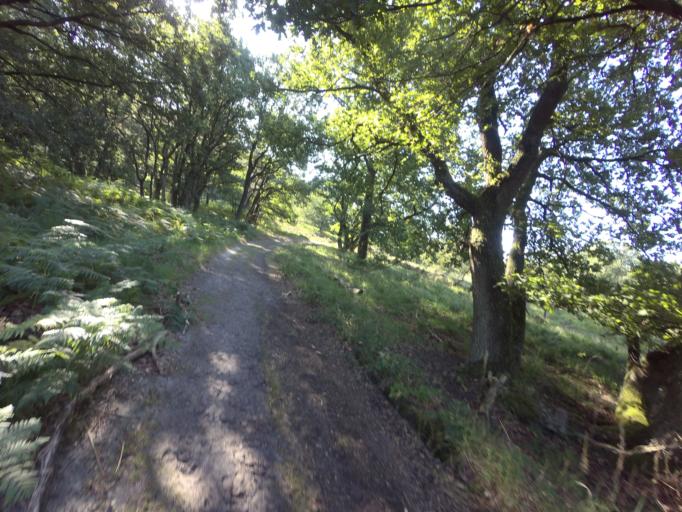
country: NL
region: Limburg
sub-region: Gemeente Roerdalen
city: Vlodrop
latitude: 51.1788
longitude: 6.1379
